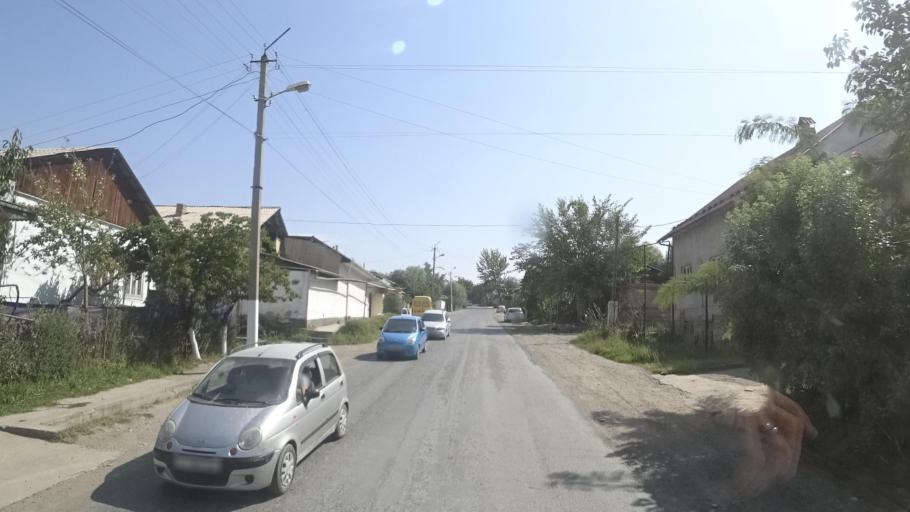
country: KG
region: Osh
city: Osh
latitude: 40.5200
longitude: 72.8176
